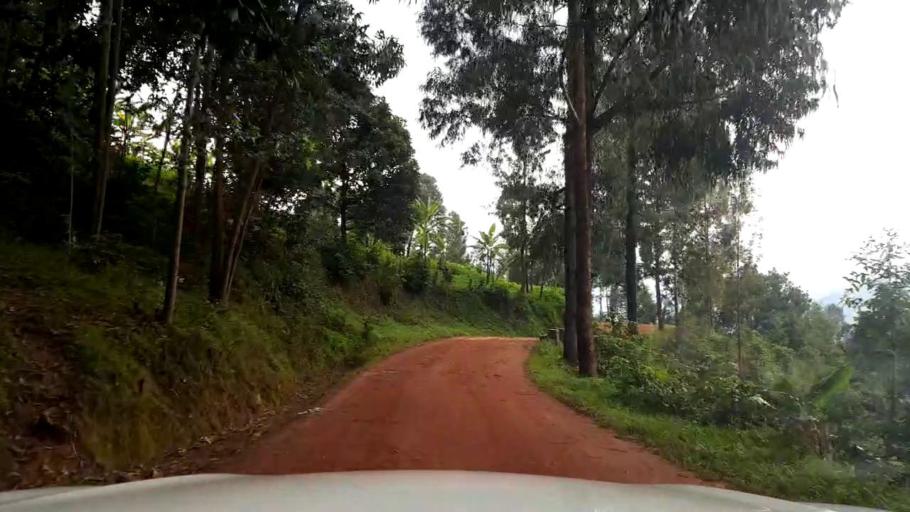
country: UG
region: Western Region
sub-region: Kisoro District
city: Kisoro
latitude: -1.3988
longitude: 29.8022
